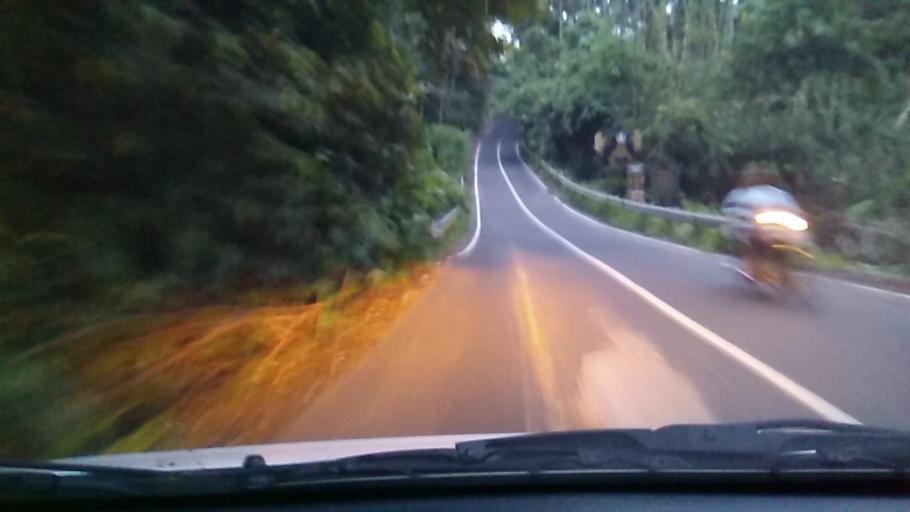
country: ID
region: Bali
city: Brahmana
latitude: -8.4735
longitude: 115.1991
